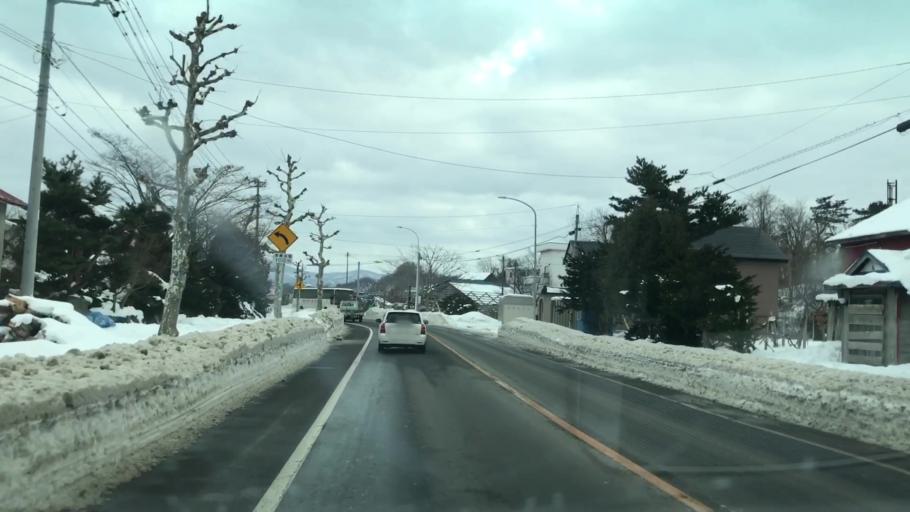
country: JP
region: Hokkaido
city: Yoichi
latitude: 43.2085
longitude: 140.7658
